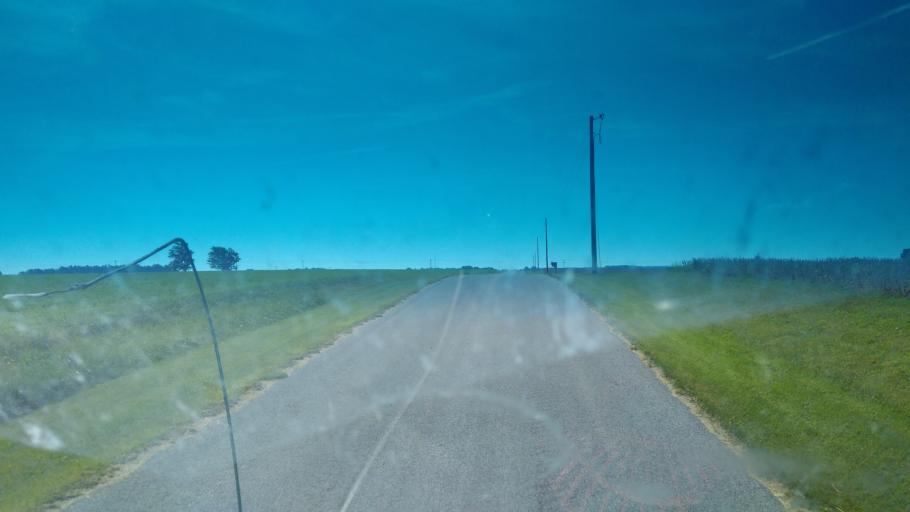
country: US
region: Ohio
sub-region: Marion County
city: Marion
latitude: 40.6620
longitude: -83.2696
